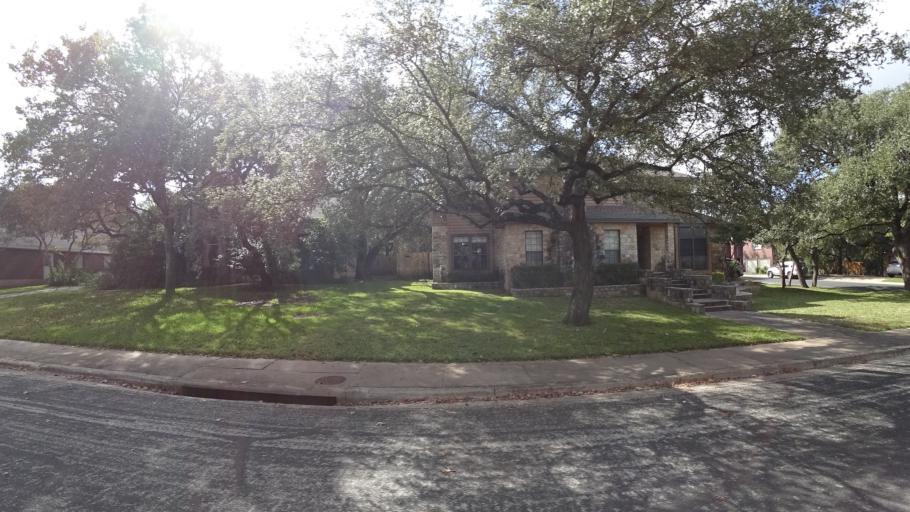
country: US
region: Texas
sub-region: Williamson County
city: Jollyville
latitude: 30.4184
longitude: -97.7894
